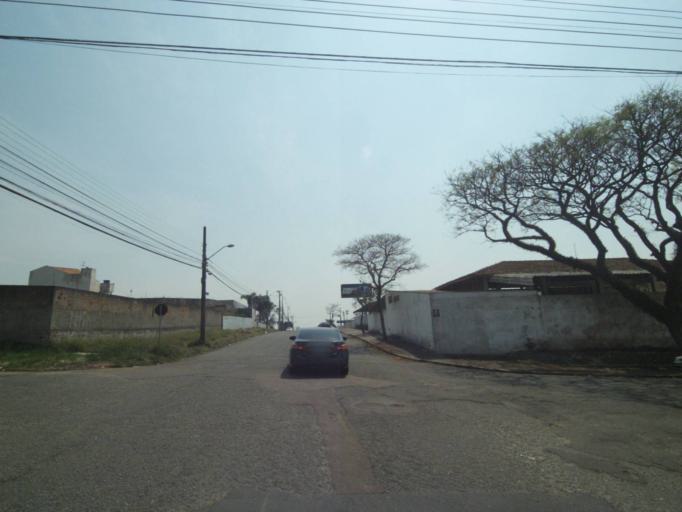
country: BR
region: Parana
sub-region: Curitiba
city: Curitiba
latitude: -25.4599
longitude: -49.2589
